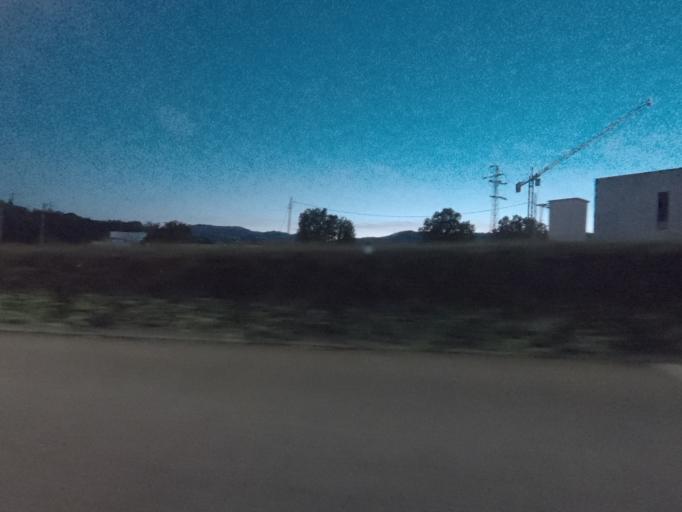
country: PT
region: Vila Real
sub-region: Vila Real
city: Vila Real
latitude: 41.2930
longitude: -7.7361
